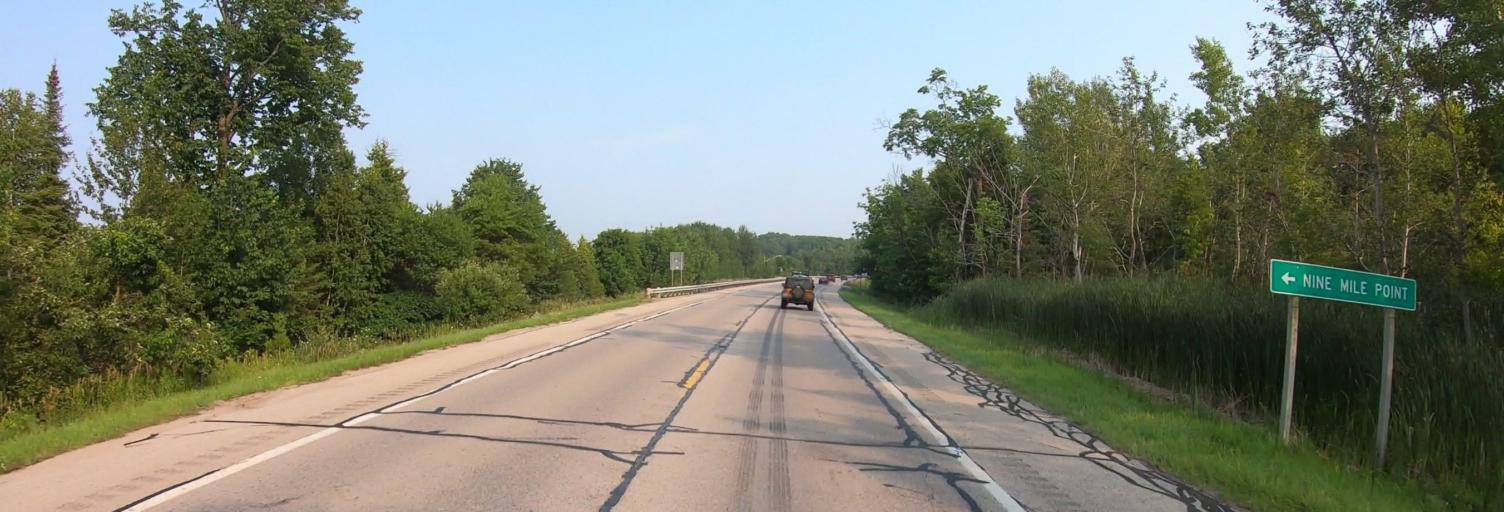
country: US
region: Michigan
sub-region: Charlevoix County
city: Charlevoix
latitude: 45.3664
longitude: -85.1249
